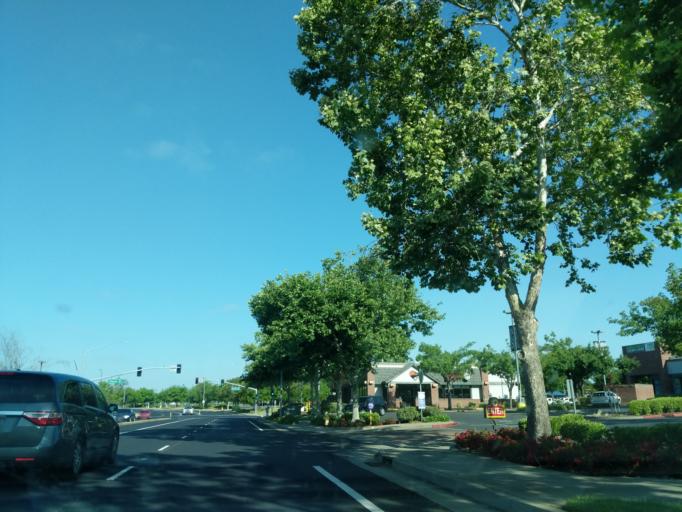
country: US
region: California
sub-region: Sacramento County
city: Folsom
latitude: 38.6705
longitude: -121.1640
